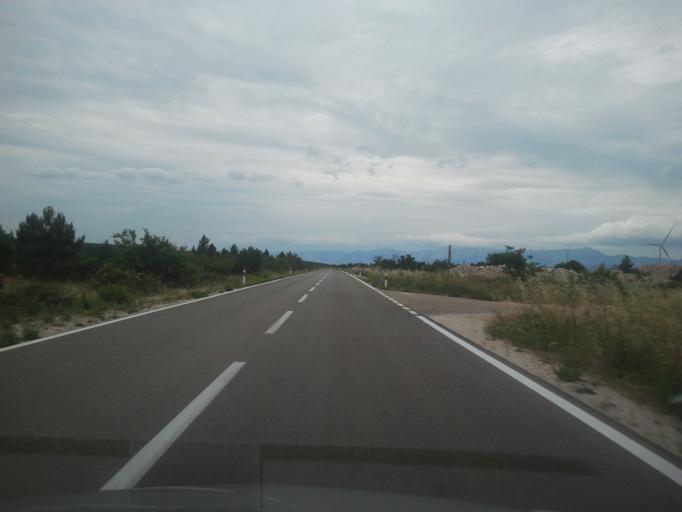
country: HR
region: Zadarska
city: Benkovac
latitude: 44.0741
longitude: 15.6009
